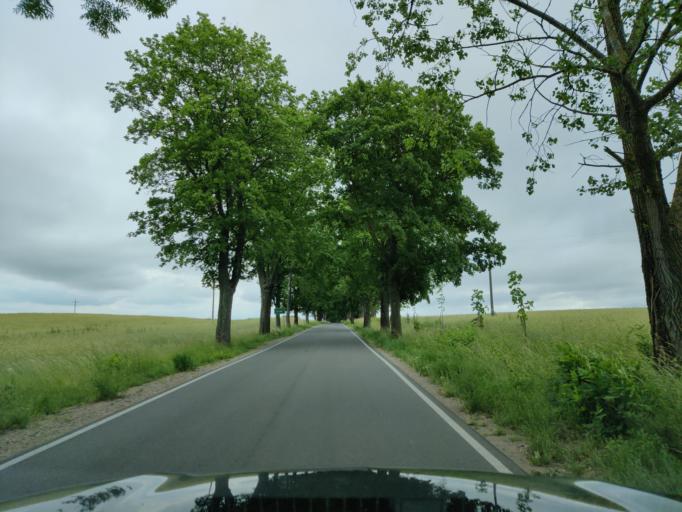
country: PL
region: Warmian-Masurian Voivodeship
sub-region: Powiat mragowski
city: Mikolajki
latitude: 53.8619
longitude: 21.6035
